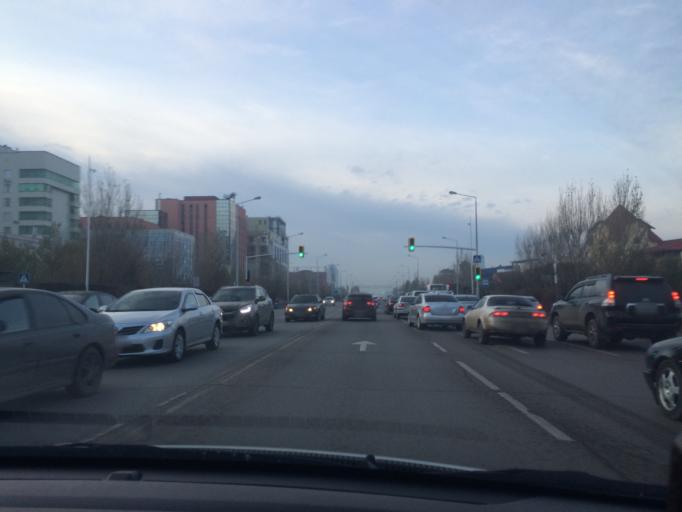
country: KZ
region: Astana Qalasy
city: Astana
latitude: 51.1443
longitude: 71.4114
